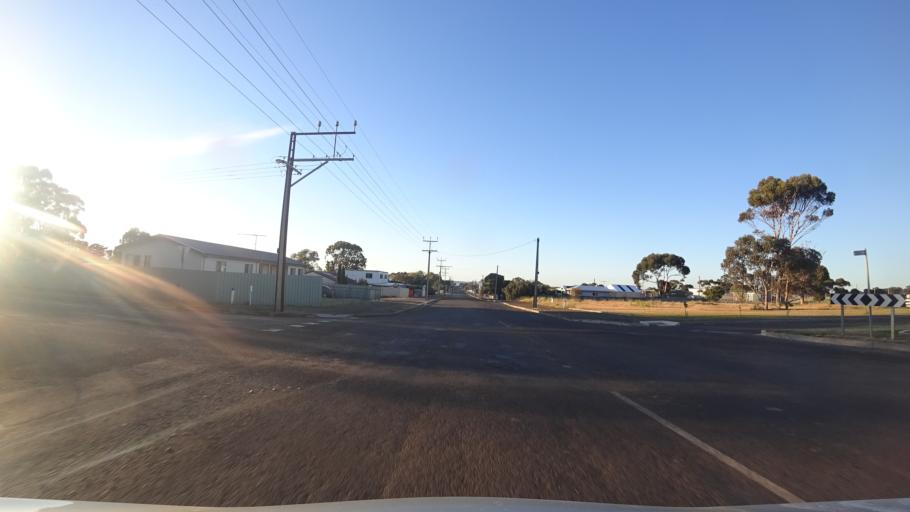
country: AU
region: South Australia
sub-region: Kangaroo Island
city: Kingscote
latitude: -35.6492
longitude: 137.6347
